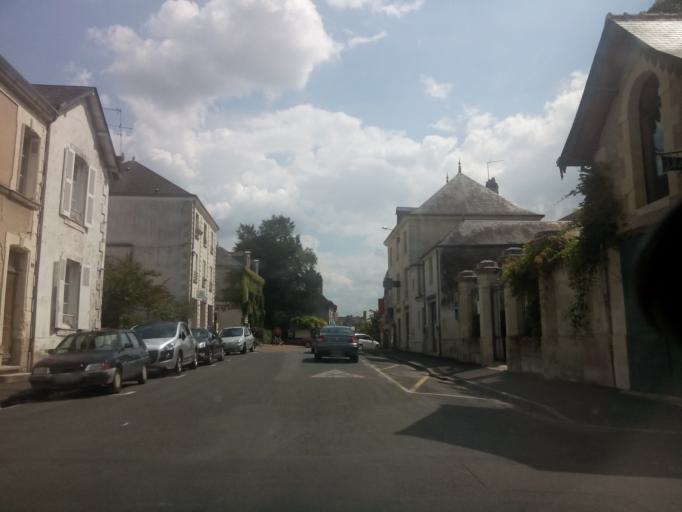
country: FR
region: Centre
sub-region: Departement d'Indre-et-Loire
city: Azay-le-Rideau
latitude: 47.2620
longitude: 0.4652
